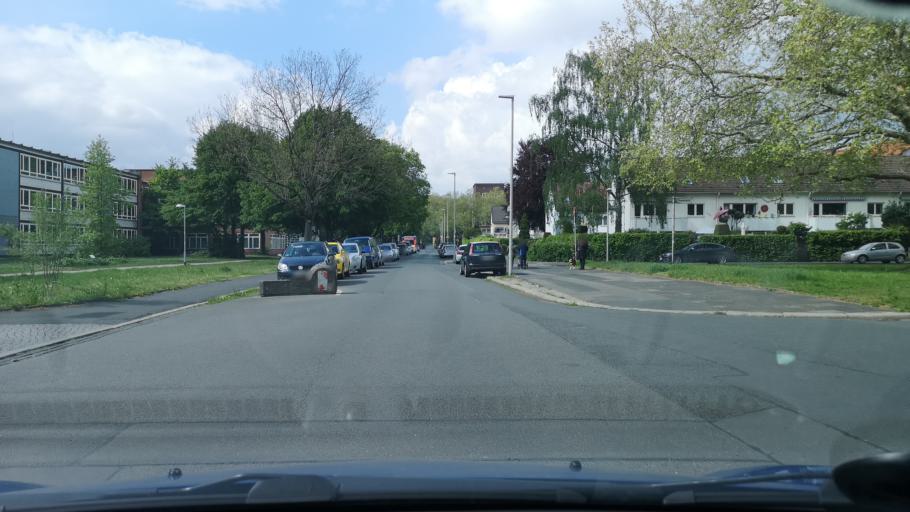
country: DE
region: Lower Saxony
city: Hannover
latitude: 52.3550
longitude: 9.7645
